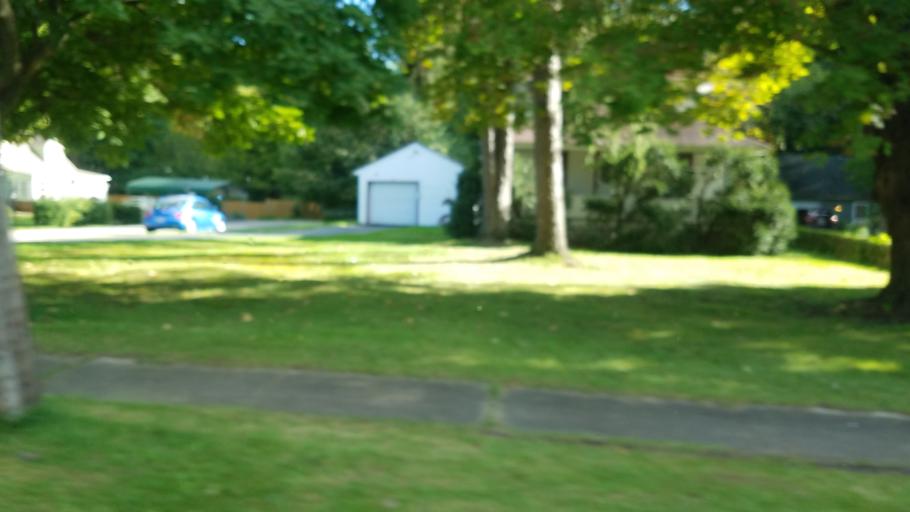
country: US
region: Ohio
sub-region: Mahoning County
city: Boardman
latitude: 41.0465
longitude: -80.6689
